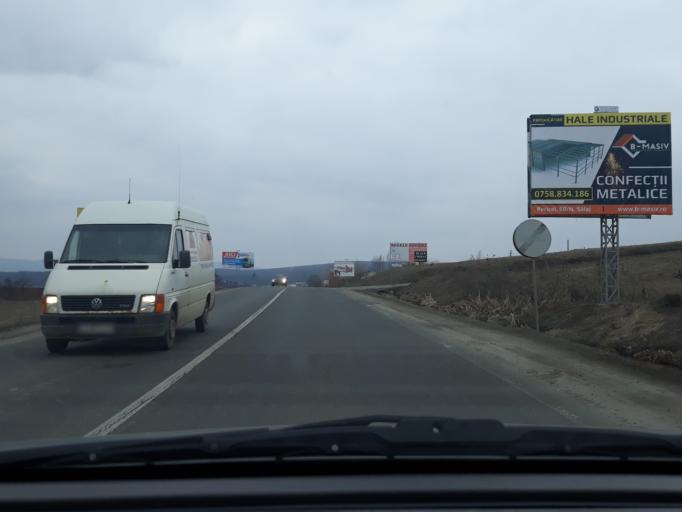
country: RO
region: Salaj
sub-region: Comuna Hereclean
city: Hereclean
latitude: 47.2378
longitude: 22.9932
